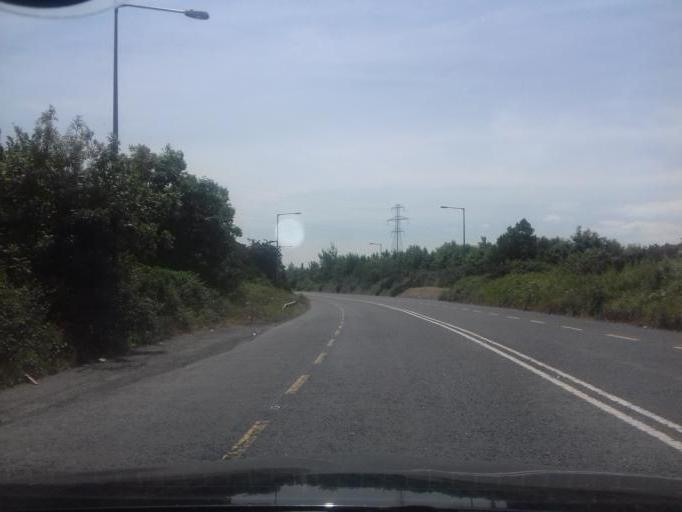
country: IE
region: Leinster
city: Balrothery
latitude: 53.5555
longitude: -6.2116
